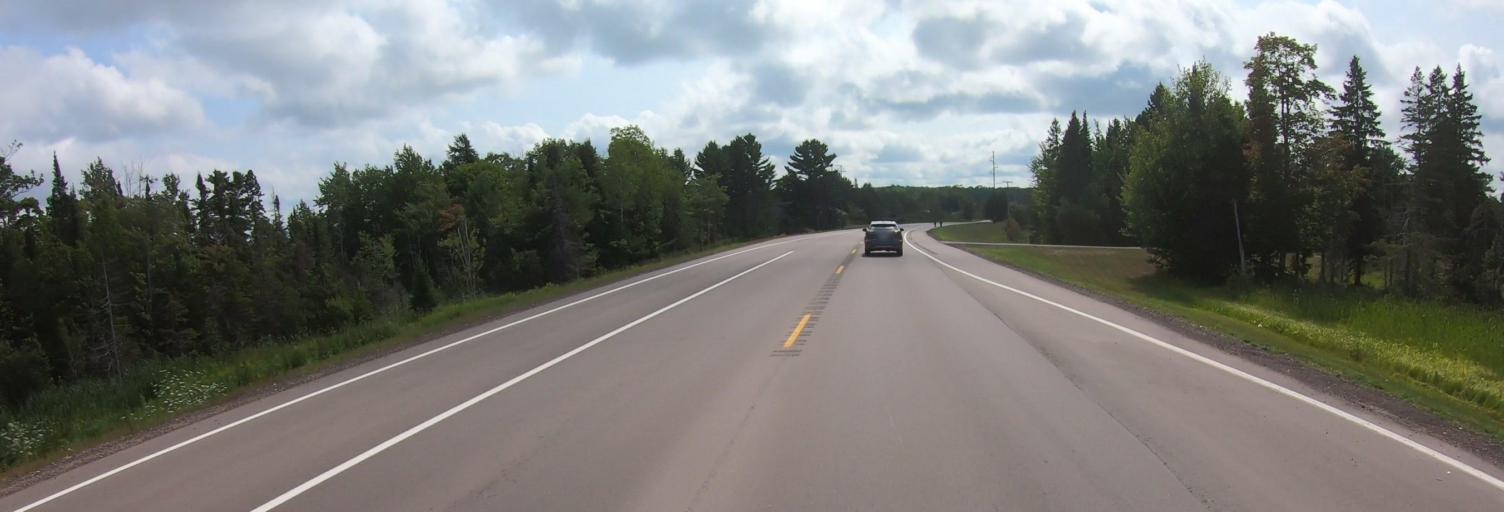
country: US
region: Michigan
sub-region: Houghton County
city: Hancock
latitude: 47.0891
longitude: -88.6269
